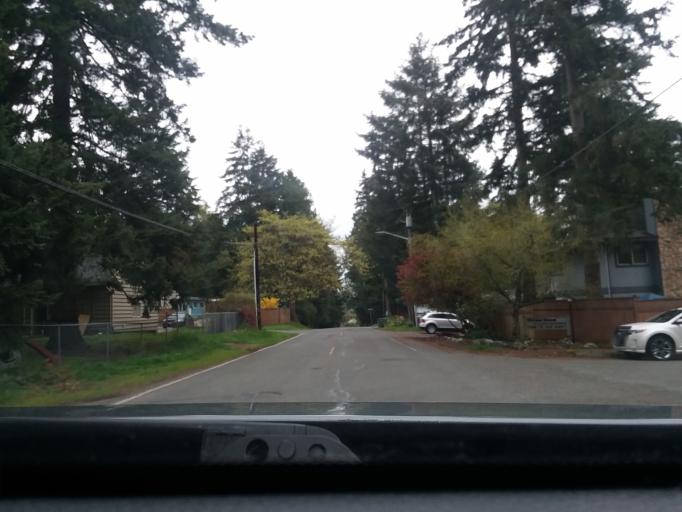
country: US
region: Washington
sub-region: Snohomish County
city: Esperance
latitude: 47.7850
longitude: -122.3396
